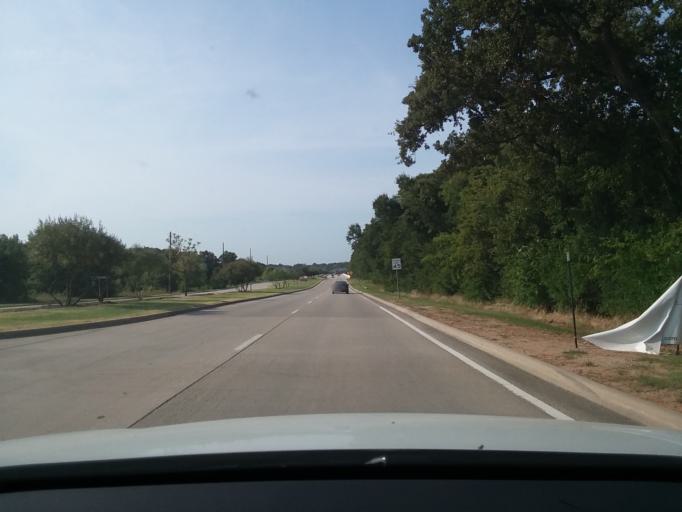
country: US
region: Texas
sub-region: Denton County
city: Copper Canyon
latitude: 33.1100
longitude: -97.0790
